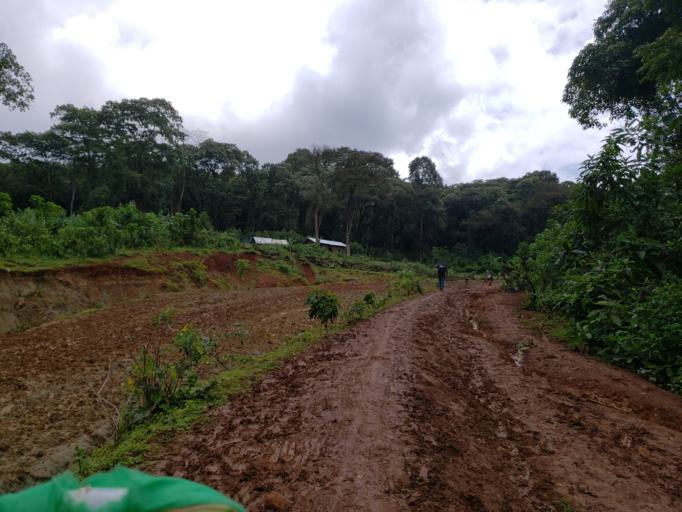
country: ET
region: Oromiya
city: Dodola
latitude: 6.4892
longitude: 39.4970
